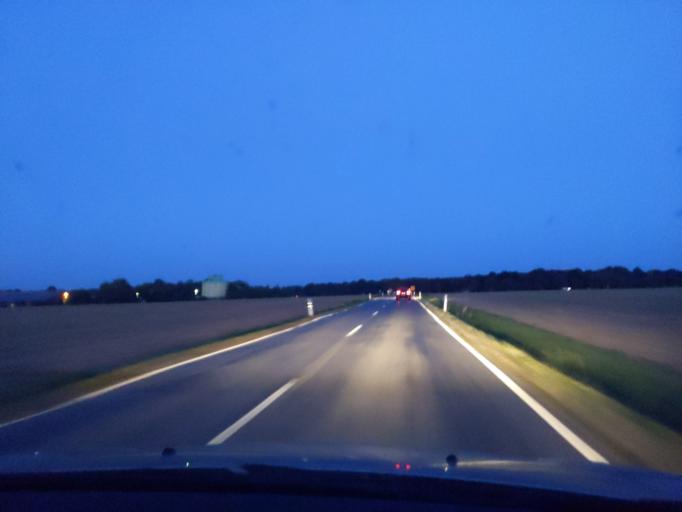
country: DE
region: Saxony
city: Guttau
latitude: 51.2540
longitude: 14.5423
